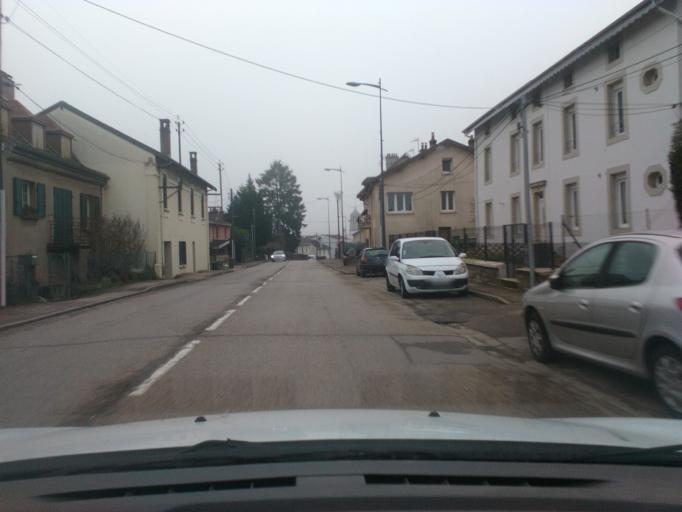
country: FR
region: Lorraine
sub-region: Departement des Vosges
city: Golbey
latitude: 48.2001
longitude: 6.4394
